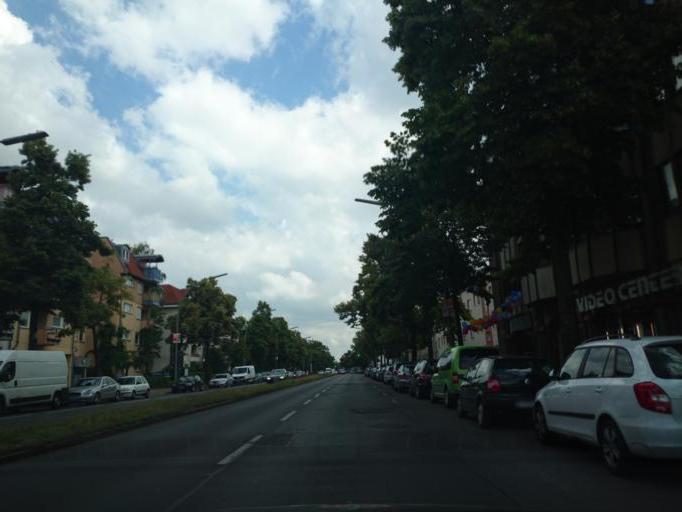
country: DE
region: Berlin
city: Lankwitz
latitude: 52.4367
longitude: 13.3465
